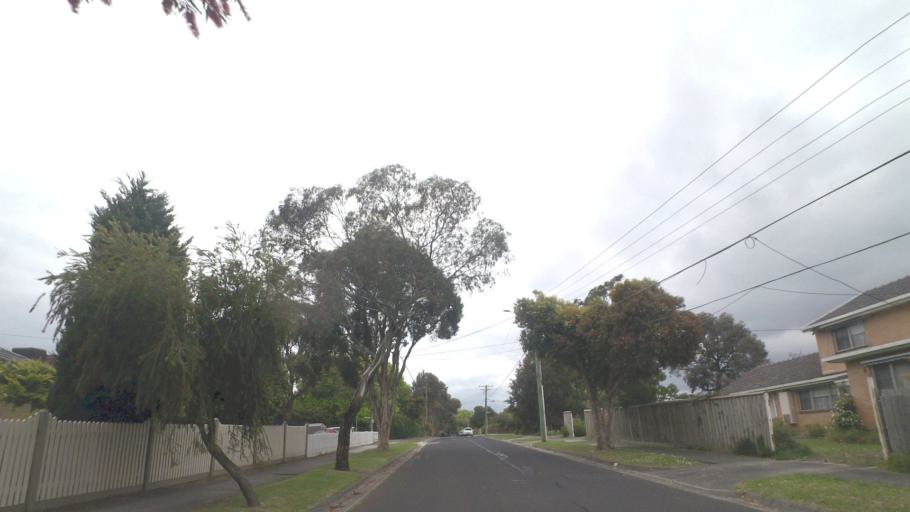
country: AU
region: Victoria
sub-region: Knox
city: Boronia
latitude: -37.8597
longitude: 145.2738
